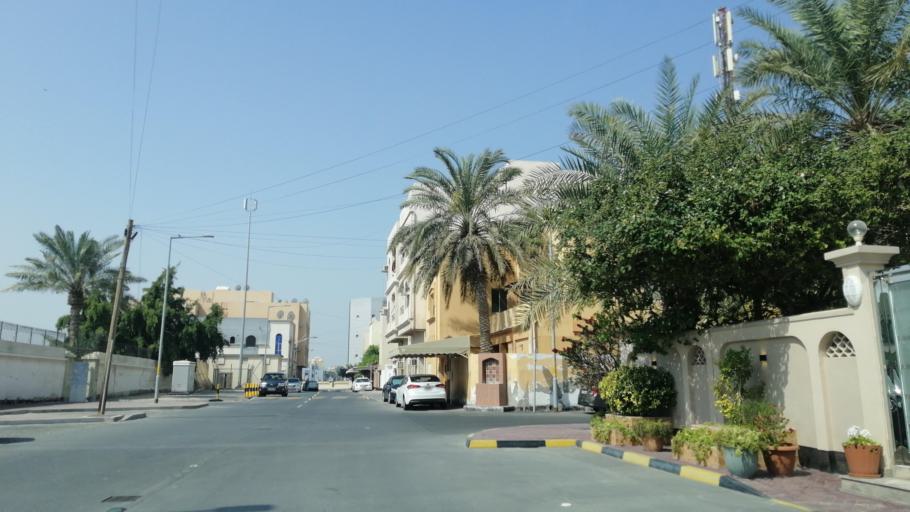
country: BH
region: Muharraq
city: Al Hadd
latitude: 26.2516
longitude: 50.6559
